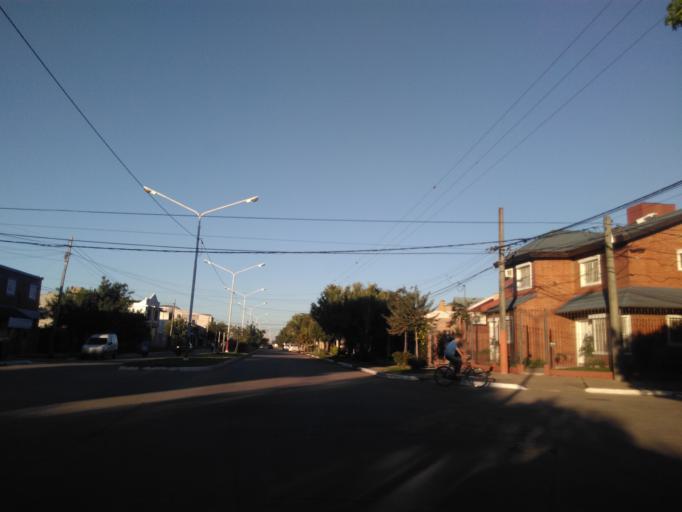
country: AR
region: Chaco
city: Resistencia
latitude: -27.4587
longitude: -59.0037
